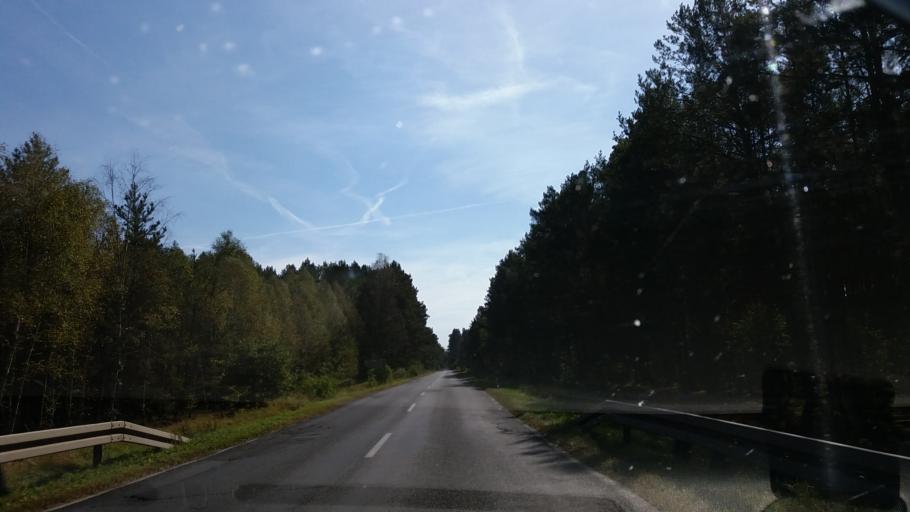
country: PL
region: Lubusz
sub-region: Powiat strzelecko-drezdenecki
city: Drezdenko
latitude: 52.7619
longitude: 15.8518
